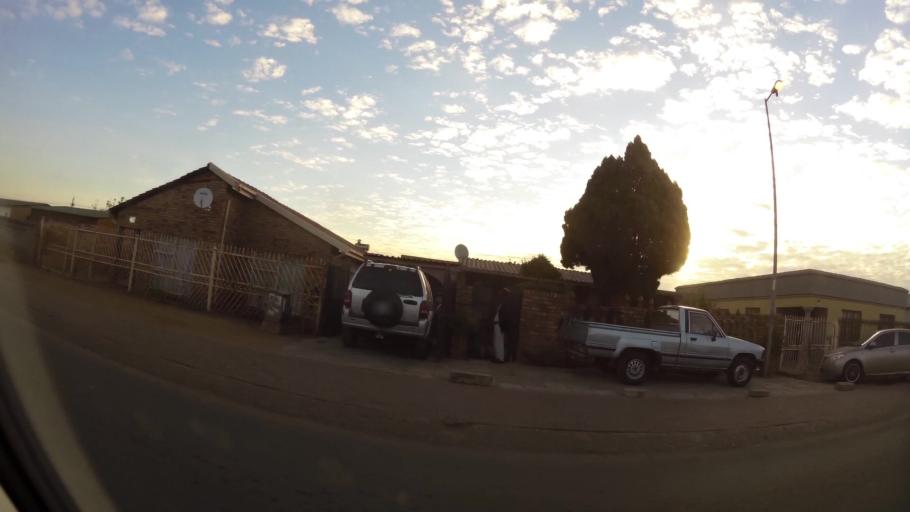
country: ZA
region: Gauteng
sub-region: City of Tshwane Metropolitan Municipality
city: Pretoria
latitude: -25.7160
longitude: 28.3449
